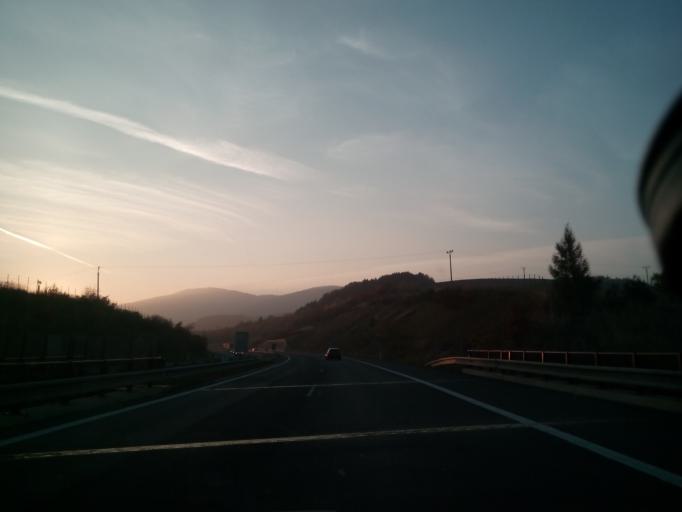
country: SK
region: Presovsky
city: Lipany
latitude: 49.0183
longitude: 20.9675
